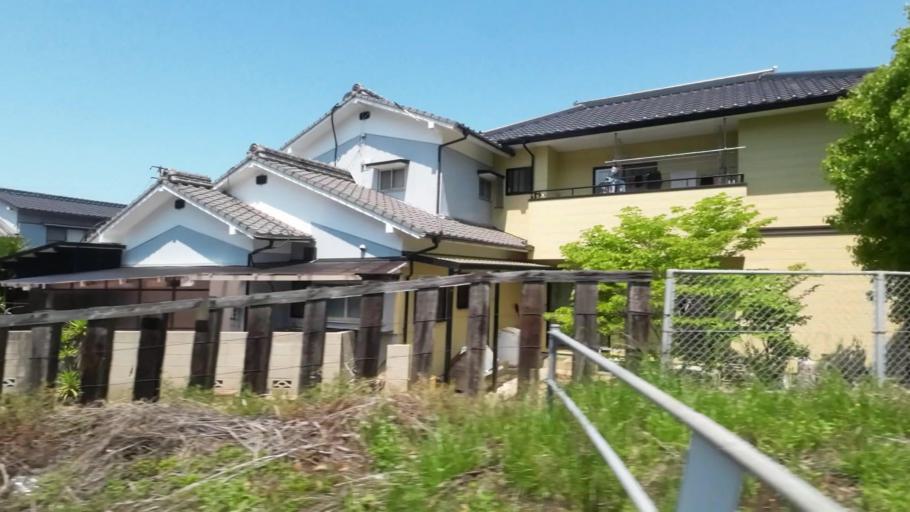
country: JP
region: Ehime
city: Hojo
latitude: 34.0095
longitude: 132.8024
